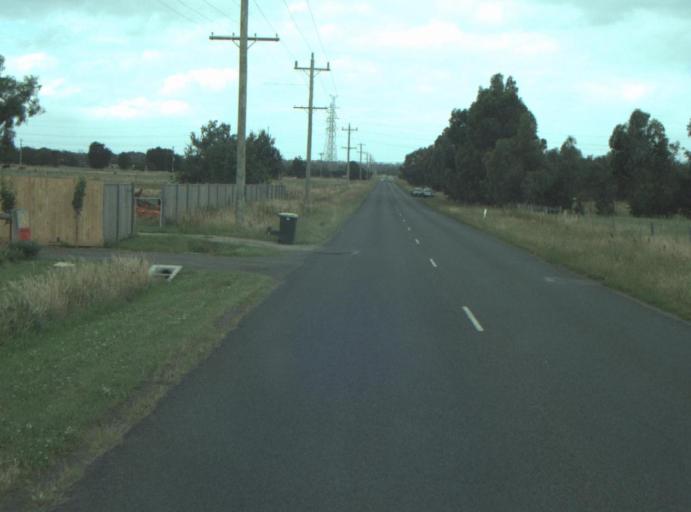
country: AU
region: Victoria
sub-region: Greater Geelong
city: Breakwater
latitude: -38.1834
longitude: 144.4089
